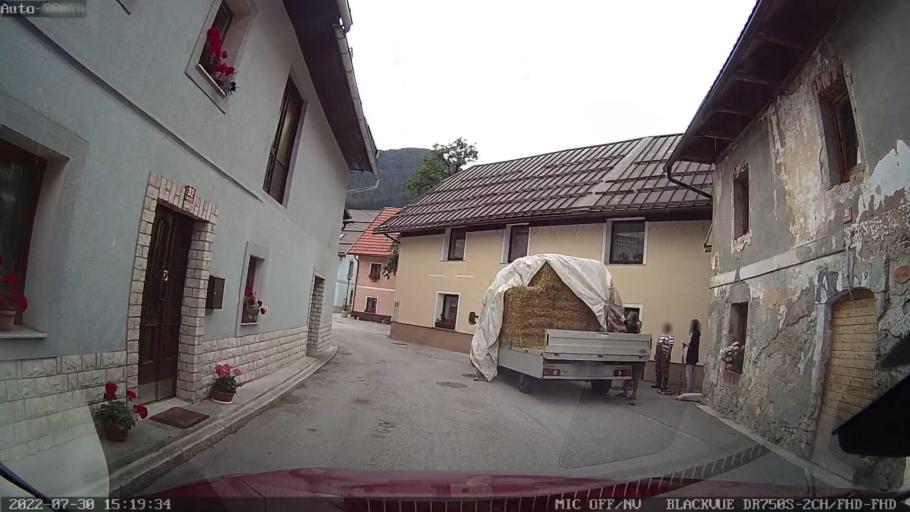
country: AT
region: Carinthia
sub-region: Politischer Bezirk Villach Land
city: Arnoldstein
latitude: 46.4978
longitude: 13.7172
